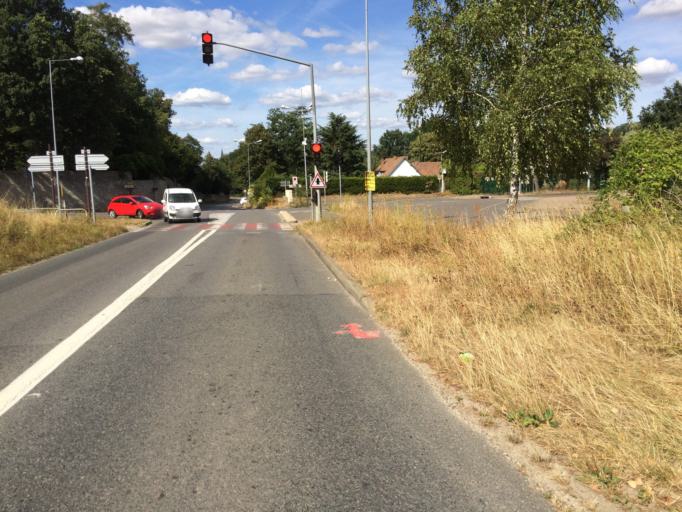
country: FR
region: Ile-de-France
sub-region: Departement de l'Essonne
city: La Ferte-Alais
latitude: 48.4758
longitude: 2.3437
